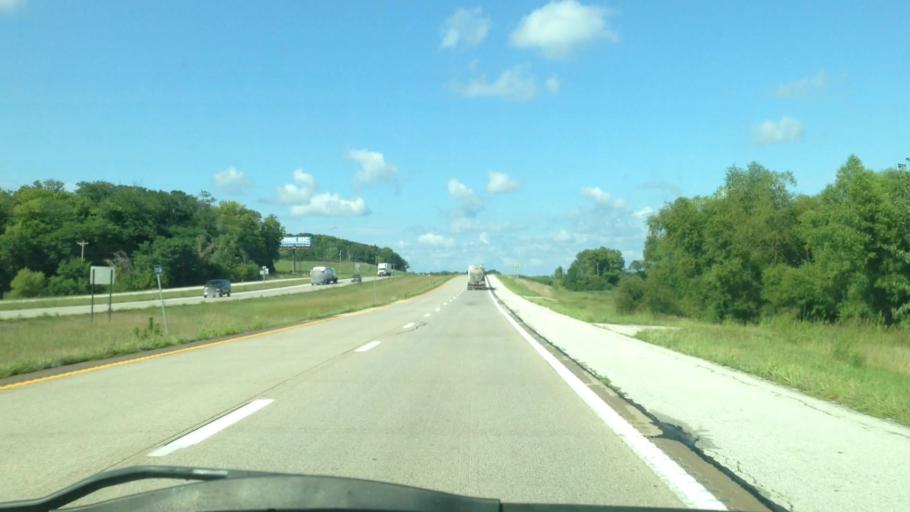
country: US
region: Missouri
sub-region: Lewis County
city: Canton
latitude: 40.1769
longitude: -91.5249
